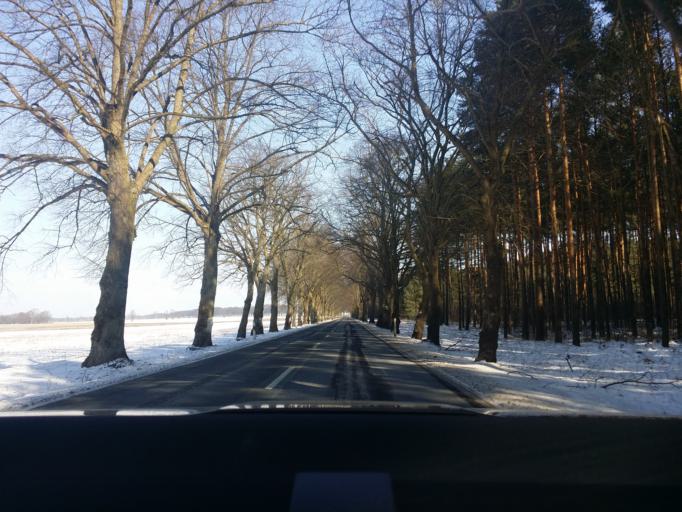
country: DE
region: Brandenburg
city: Wittstock
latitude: 53.1991
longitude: 12.5714
